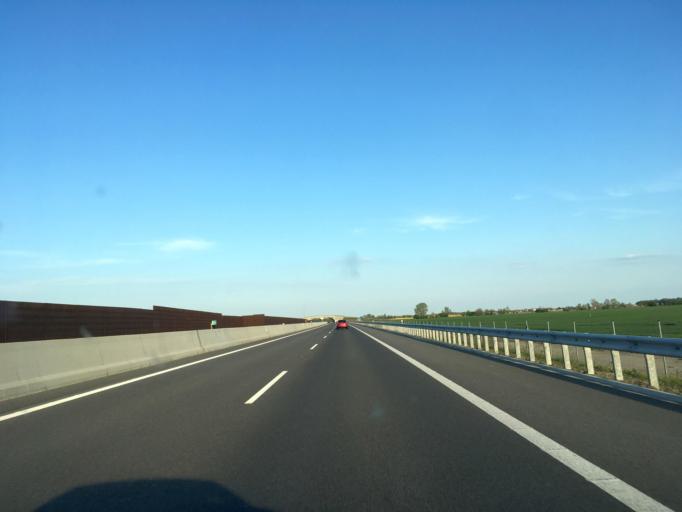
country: SK
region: Trnavsky
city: Samorin
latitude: 48.0269
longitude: 17.3787
